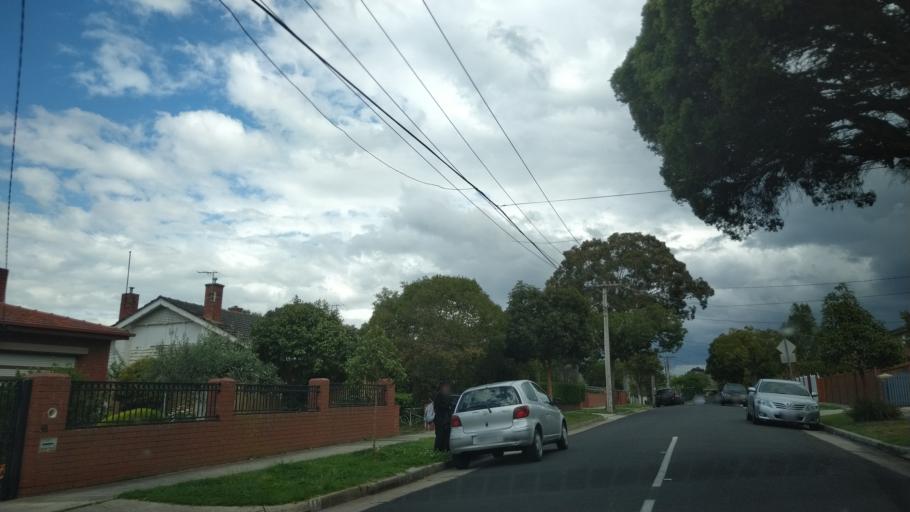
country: AU
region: Victoria
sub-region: Glen Eira
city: Murrumbeena
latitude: -37.8925
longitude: 145.0649
